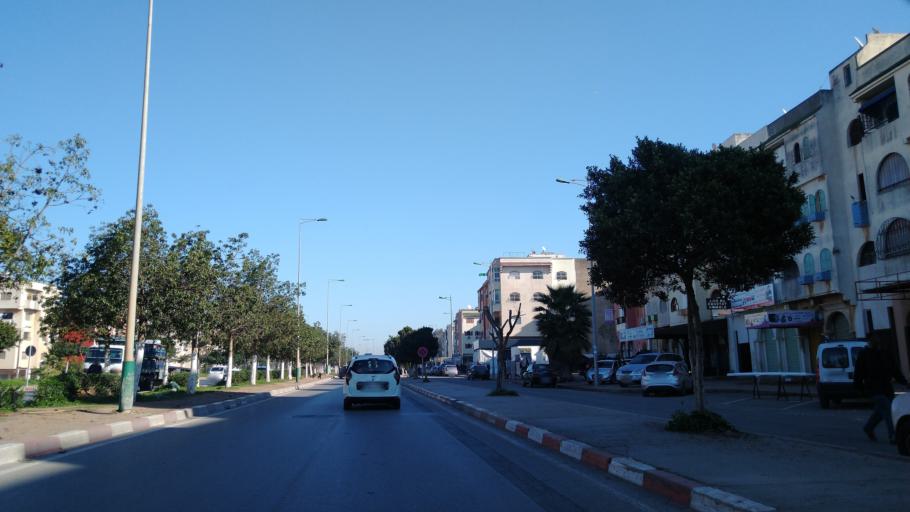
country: MA
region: Rabat-Sale-Zemmour-Zaer
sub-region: Skhirate-Temara
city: Temara
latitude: 33.9279
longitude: -6.8924
